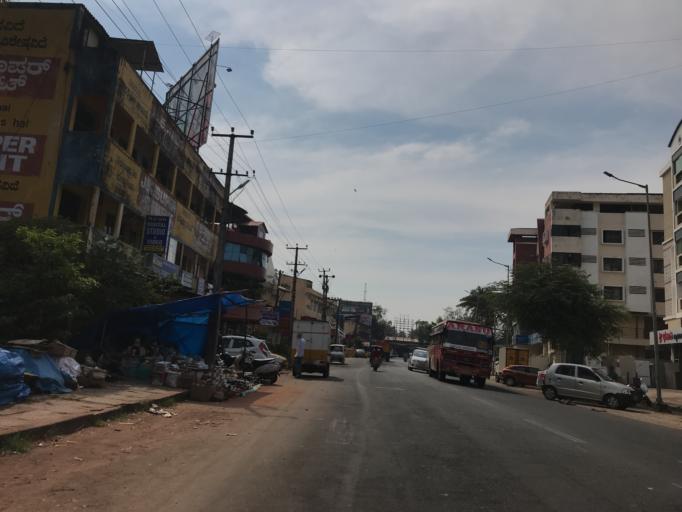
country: IN
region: Karnataka
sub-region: Dakshina Kannada
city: Ullal
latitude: 12.8498
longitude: 74.8479
